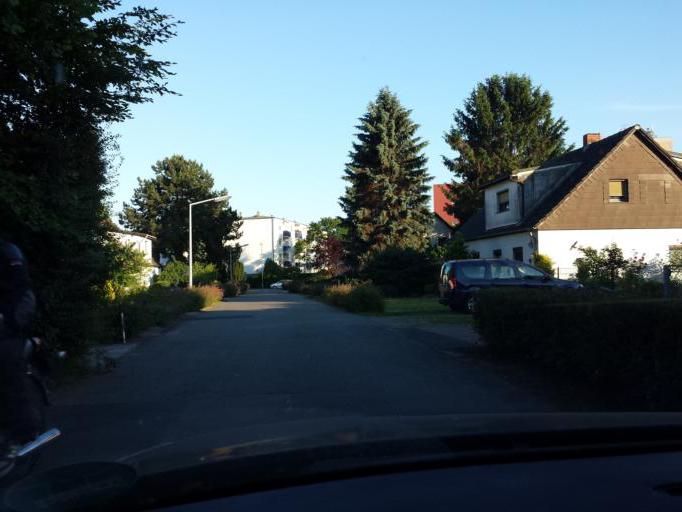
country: DE
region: Berlin
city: Lichtenrade
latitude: 52.4188
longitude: 13.4097
